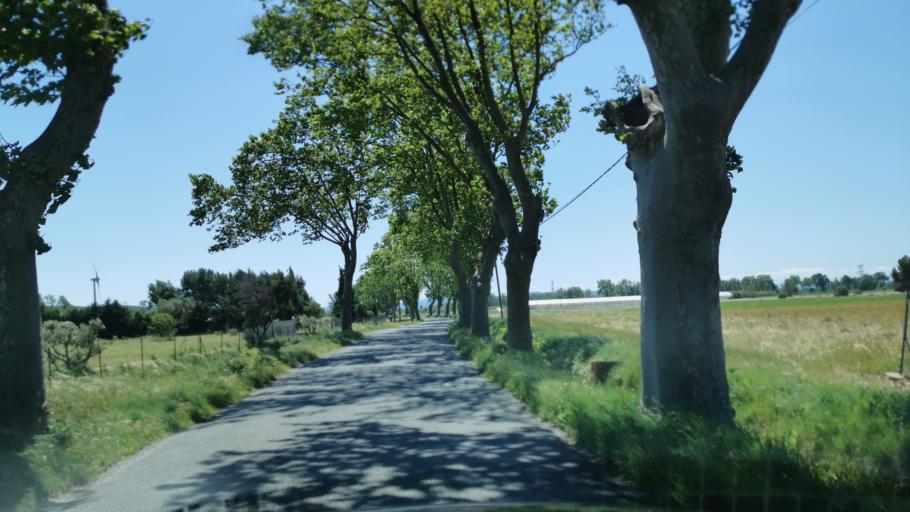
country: FR
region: Languedoc-Roussillon
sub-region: Departement de l'Aude
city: Canet
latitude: 43.2161
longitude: 2.8450
